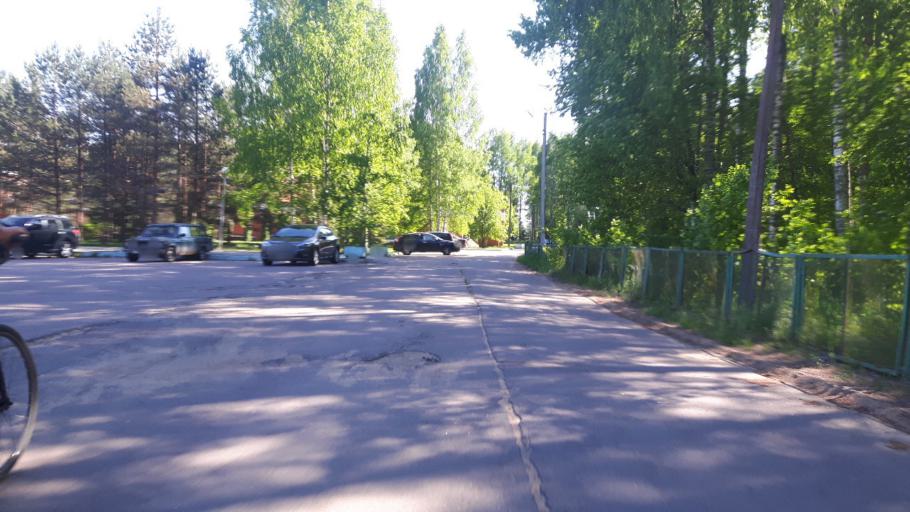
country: RU
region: Leningrad
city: Sista-Palkino
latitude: 59.7640
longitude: 28.7400
